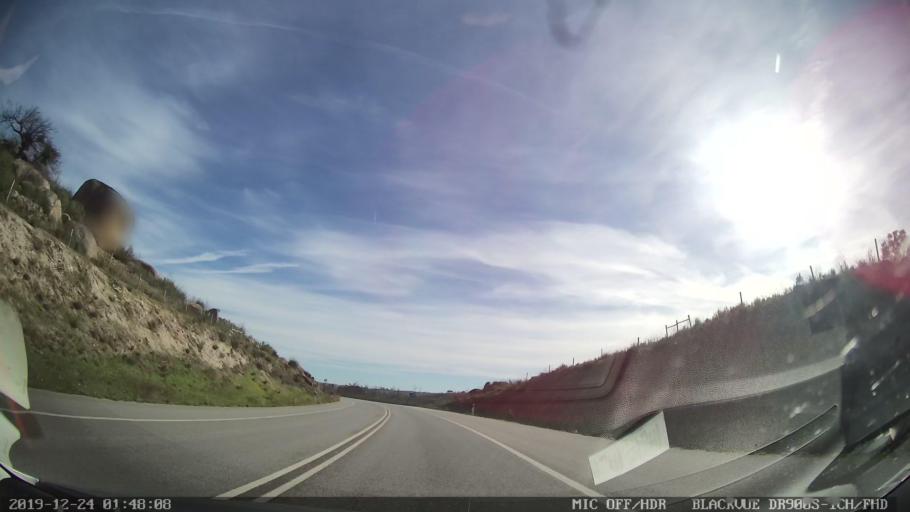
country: PT
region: Portalegre
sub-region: Nisa
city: Nisa
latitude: 39.5235
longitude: -7.7826
